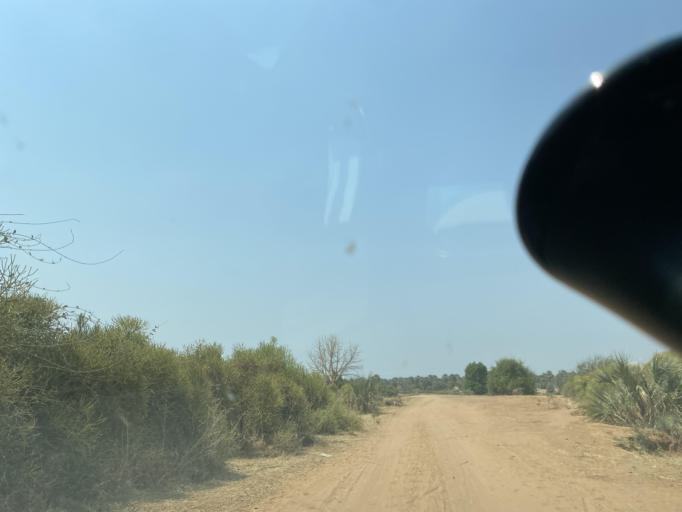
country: ZW
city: Chirundu
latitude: -16.1524
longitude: 28.8054
